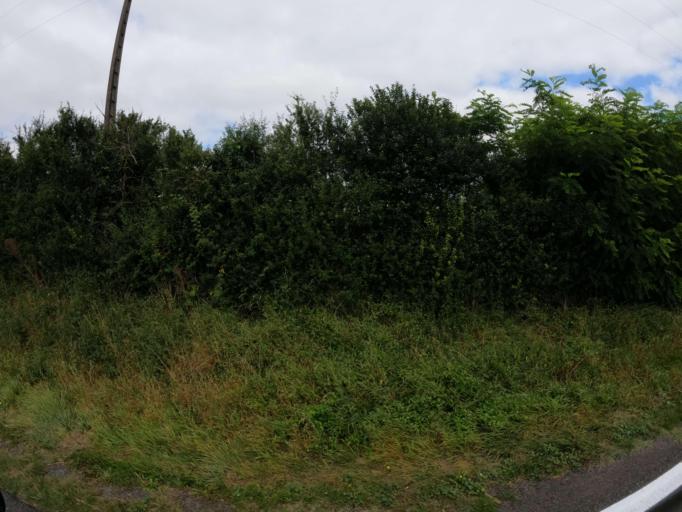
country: FR
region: Poitou-Charentes
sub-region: Departement de la Vienne
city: Savigne
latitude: 46.1594
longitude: 0.3487
